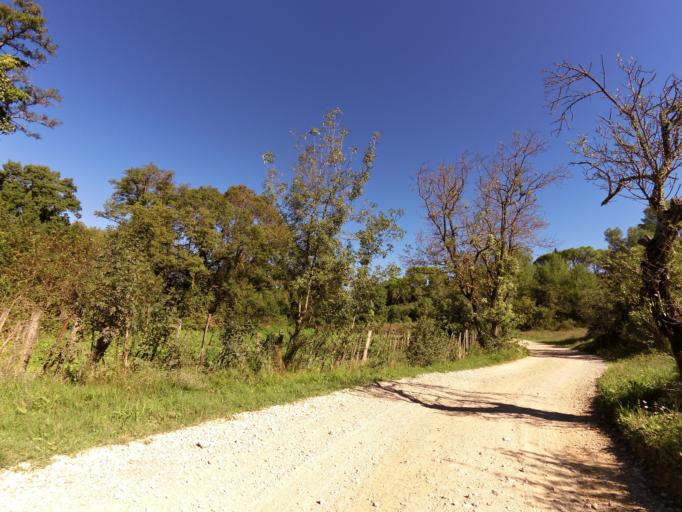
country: FR
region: Languedoc-Roussillon
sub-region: Departement du Gard
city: Aubais
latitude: 43.7488
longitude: 4.1410
